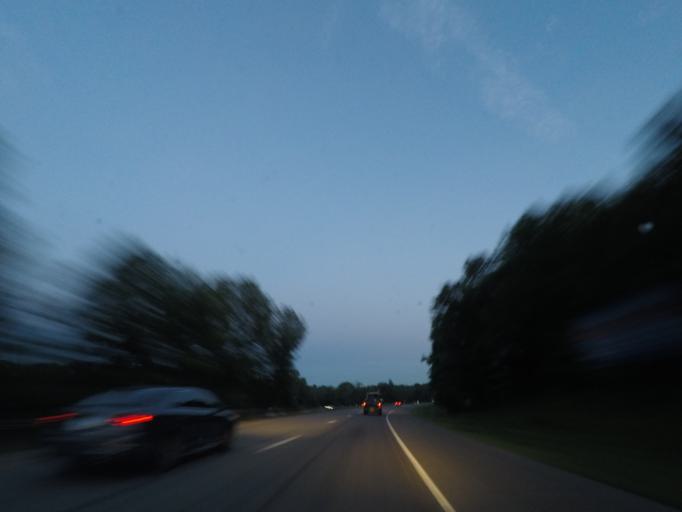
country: US
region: Connecticut
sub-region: Windham County
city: Putnam
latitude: 41.8937
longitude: -71.8967
